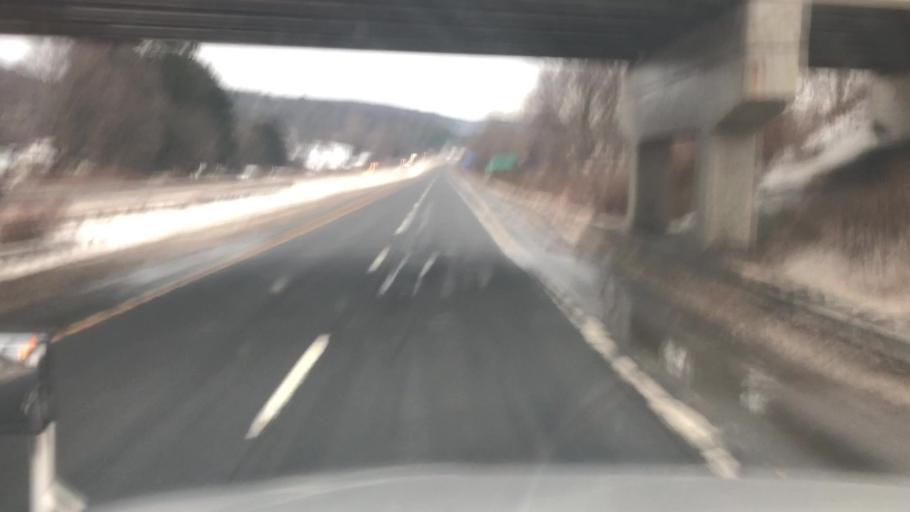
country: US
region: Pennsylvania
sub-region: Susquehanna County
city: Hallstead
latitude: 41.9817
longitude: -75.7458
